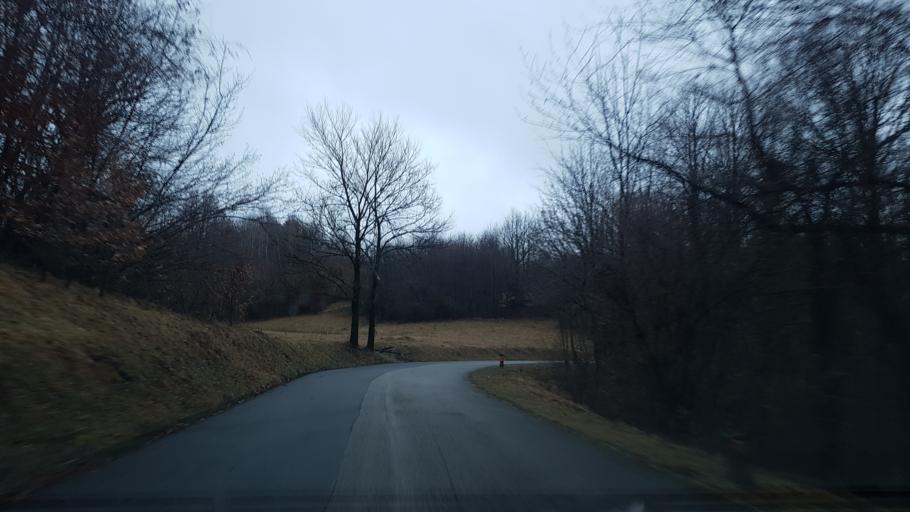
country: IT
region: Friuli Venezia Giulia
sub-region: Provincia di Udine
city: Stregna
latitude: 46.1185
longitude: 13.5848
